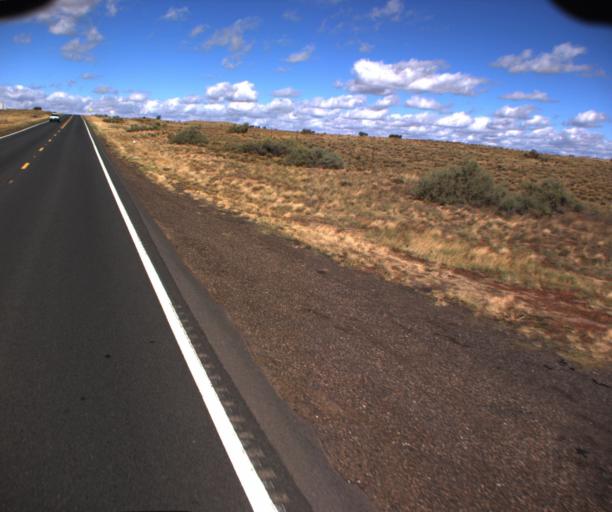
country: US
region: Arizona
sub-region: Apache County
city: Houck
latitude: 35.0309
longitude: -109.2543
